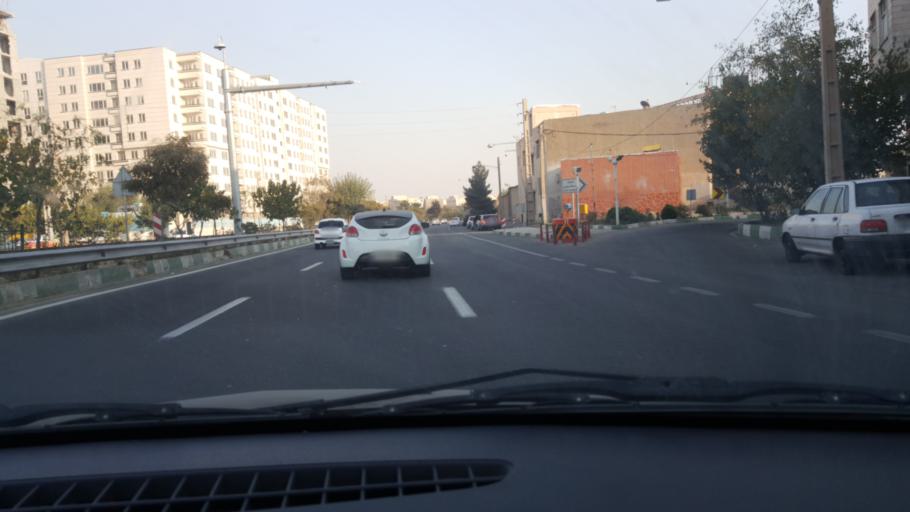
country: IR
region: Tehran
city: Tehran
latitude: 35.7398
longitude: 51.2788
